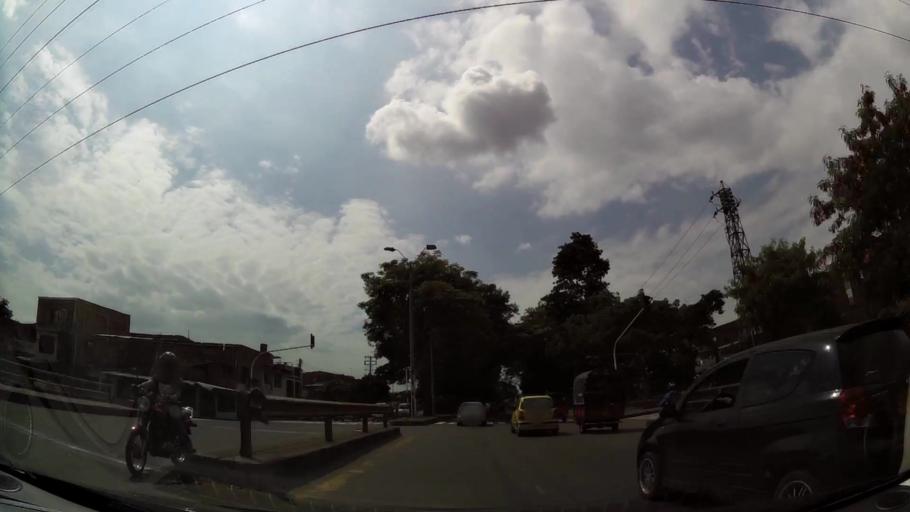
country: CO
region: Valle del Cauca
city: Cali
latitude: 3.4846
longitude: -76.4862
